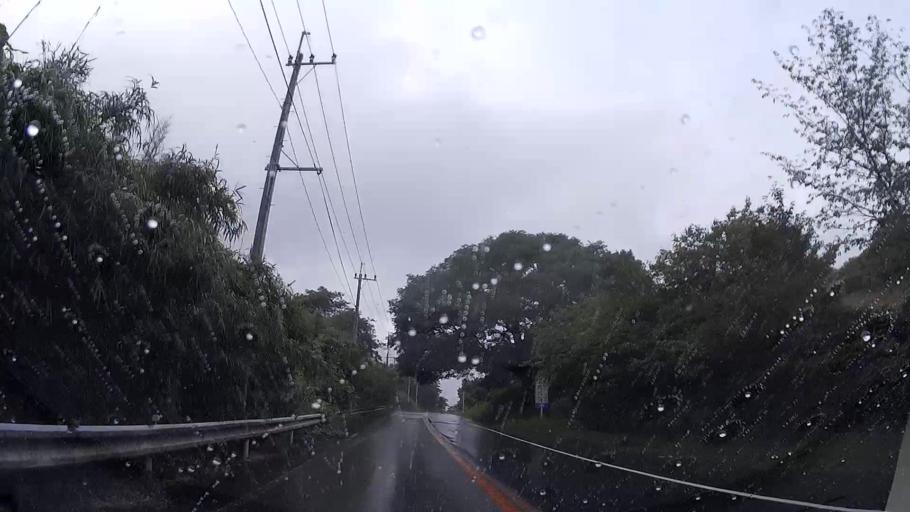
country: JP
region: Kumamoto
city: Aso
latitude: 32.8724
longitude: 130.9933
